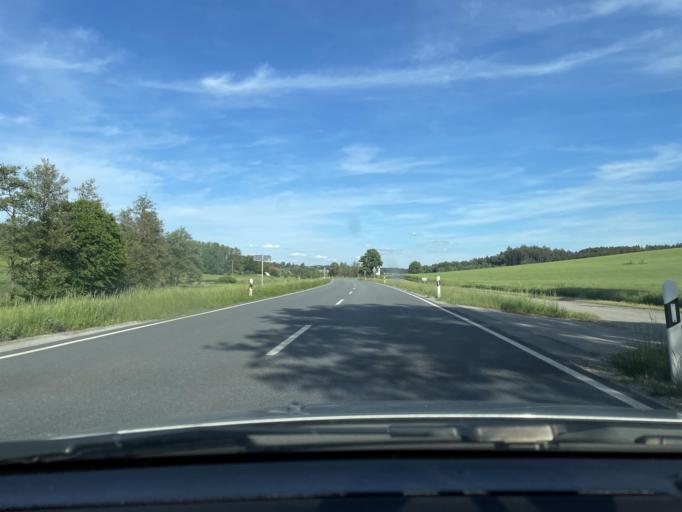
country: DE
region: Bavaria
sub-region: Lower Bavaria
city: Furth
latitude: 48.6089
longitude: 12.0201
